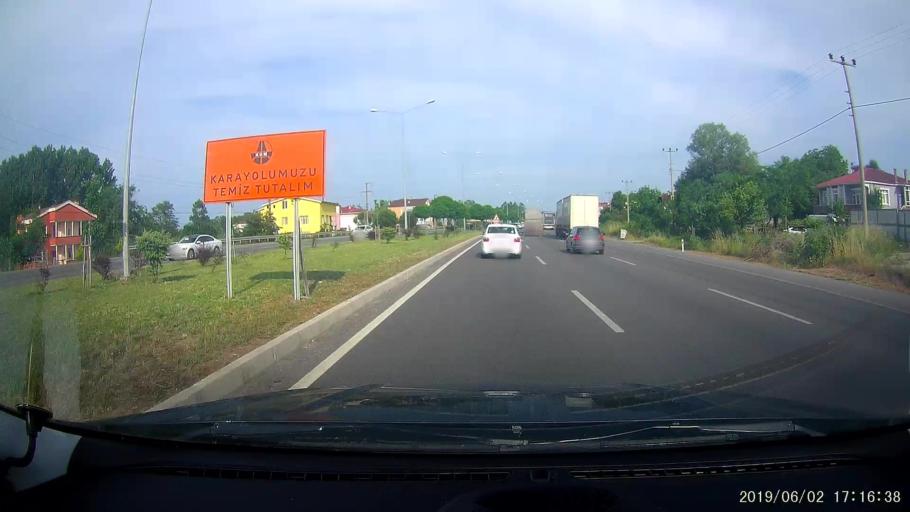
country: TR
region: Samsun
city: Dikbiyik
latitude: 41.2336
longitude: 36.5694
